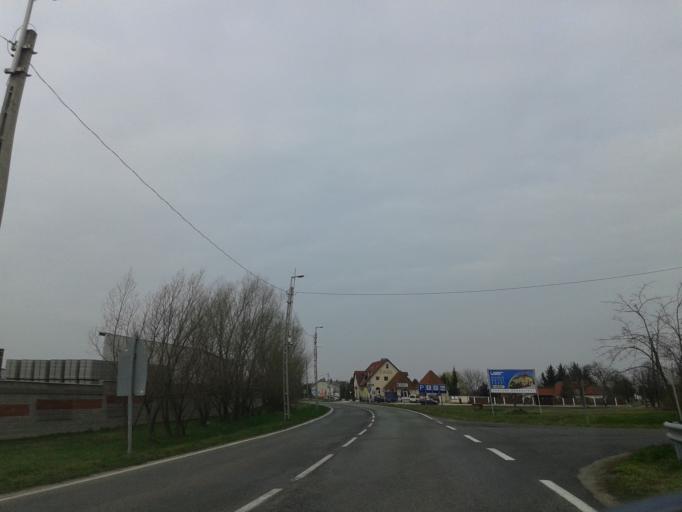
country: HU
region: Gyor-Moson-Sopron
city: Bony
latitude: 47.7330
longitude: 17.8435
